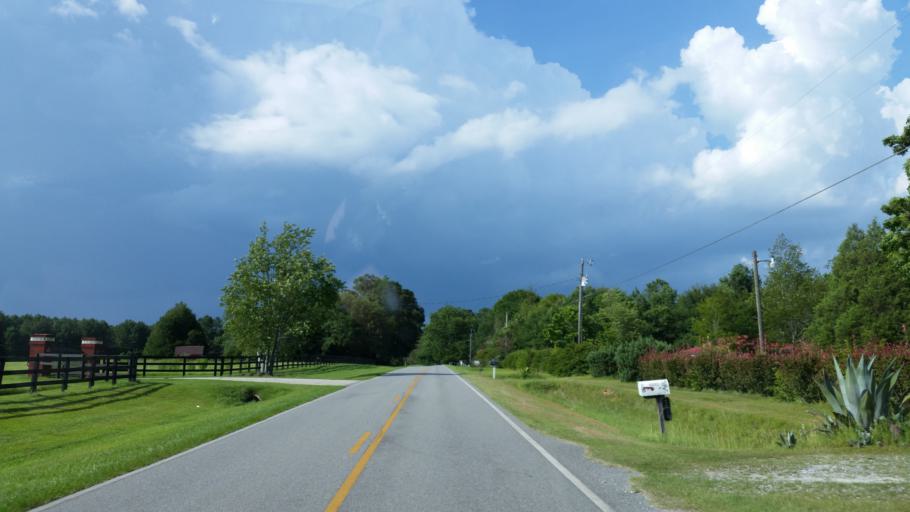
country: US
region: Georgia
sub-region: Lowndes County
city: Hahira
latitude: 30.9713
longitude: -83.3989
